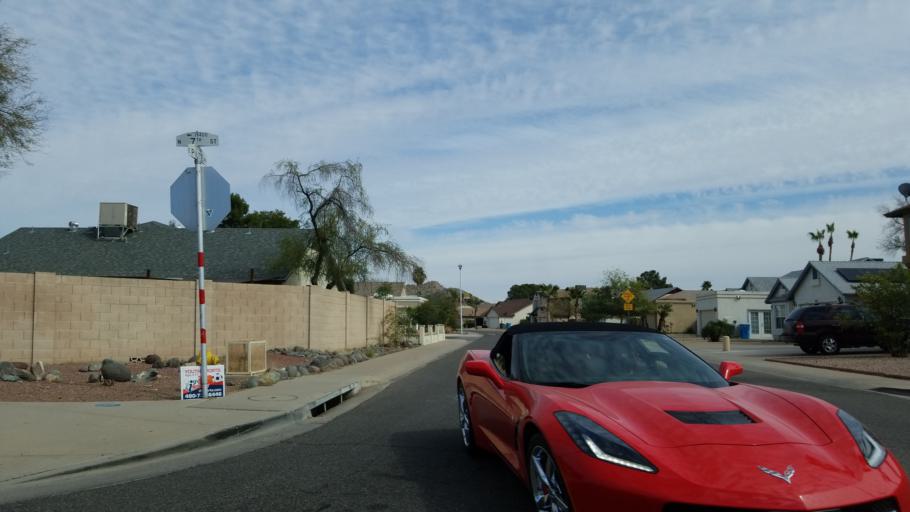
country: US
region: Arizona
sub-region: Maricopa County
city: Glendale
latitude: 33.6629
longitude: -112.0655
